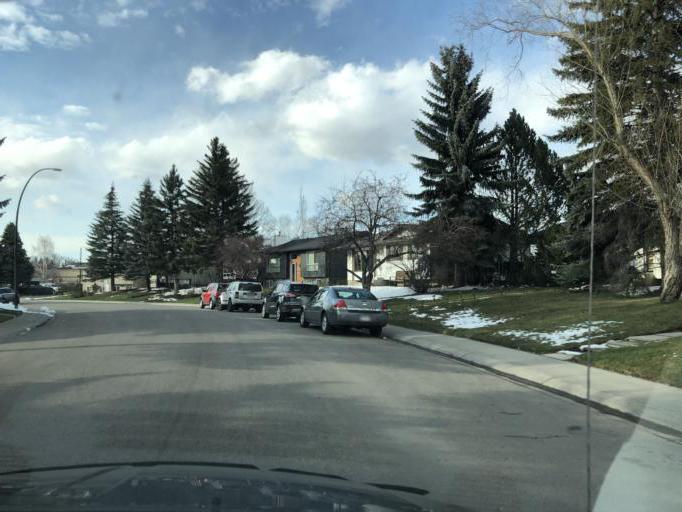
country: CA
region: Alberta
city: Calgary
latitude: 50.9451
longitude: -114.0290
